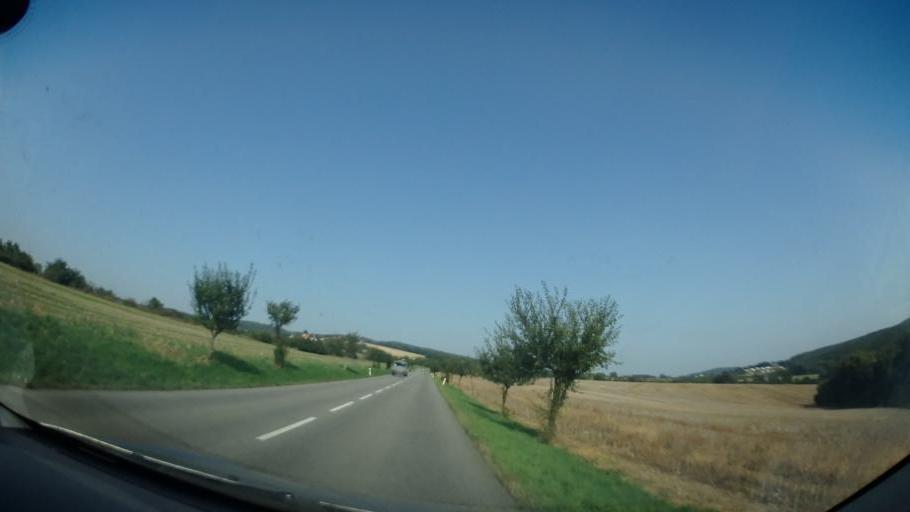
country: CZ
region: South Moravian
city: Kurim
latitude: 49.2485
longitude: 16.5274
